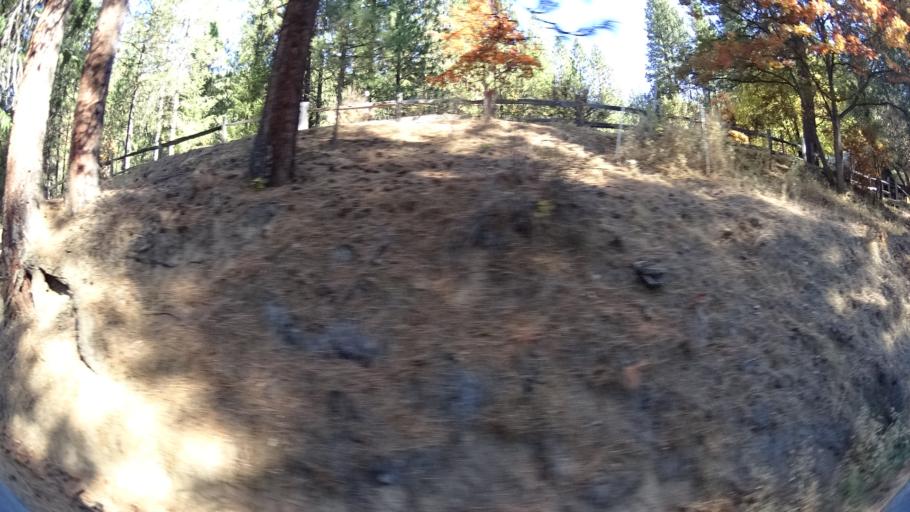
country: US
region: California
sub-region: Siskiyou County
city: Yreka
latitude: 41.6361
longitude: -122.9678
